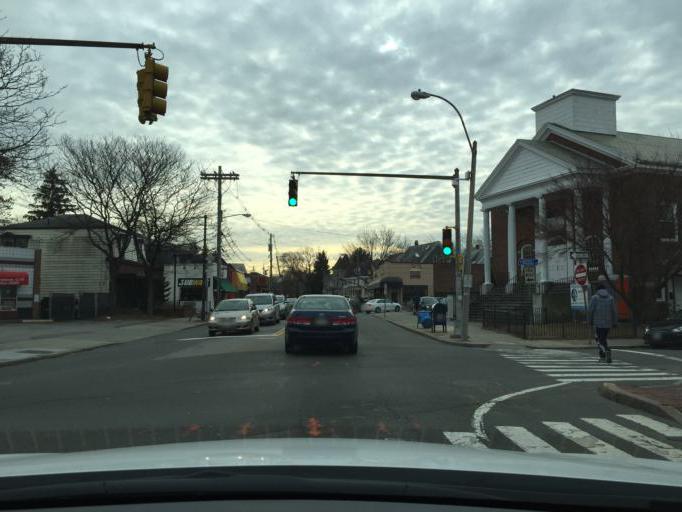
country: US
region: Massachusetts
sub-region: Middlesex County
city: Somerville
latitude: 42.3940
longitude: -71.1210
